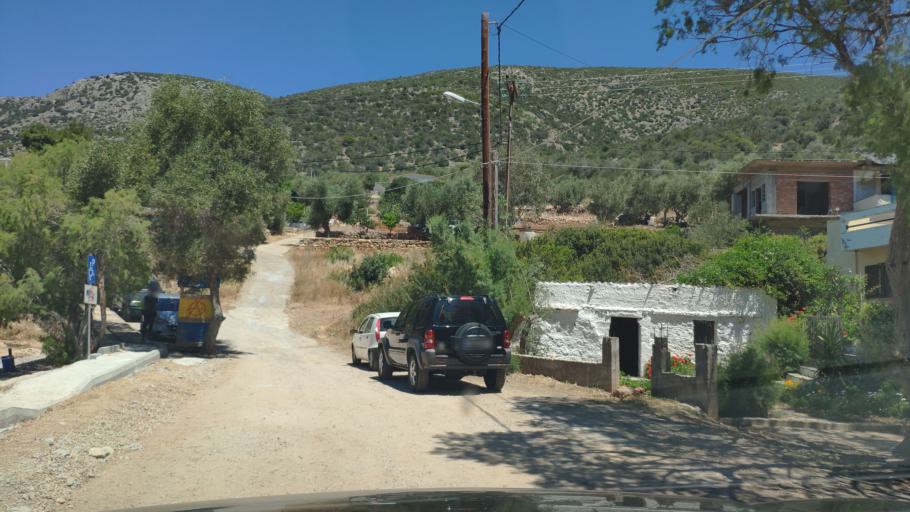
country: GR
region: Central Greece
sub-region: Nomos Voiotias
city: Kaparellion
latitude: 38.1832
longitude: 23.1430
